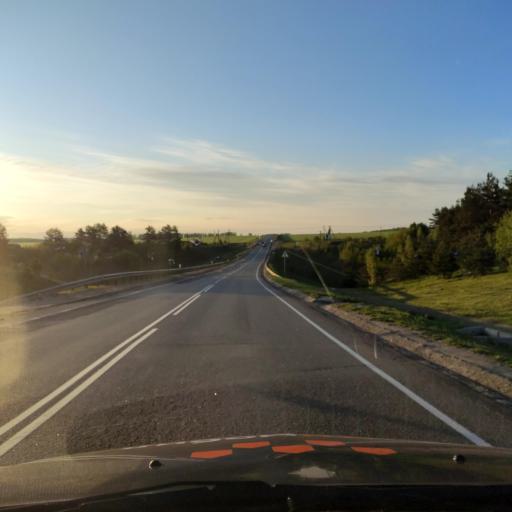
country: RU
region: Orjol
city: Livny
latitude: 52.4494
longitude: 37.5107
